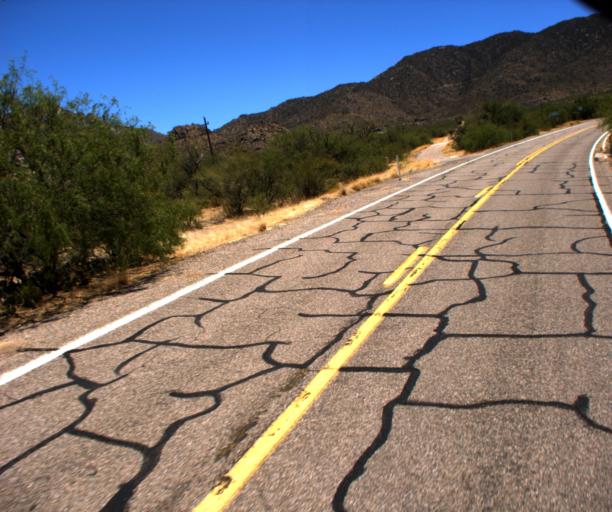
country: US
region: Arizona
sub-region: Pima County
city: Three Points
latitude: 31.9993
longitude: -111.5711
